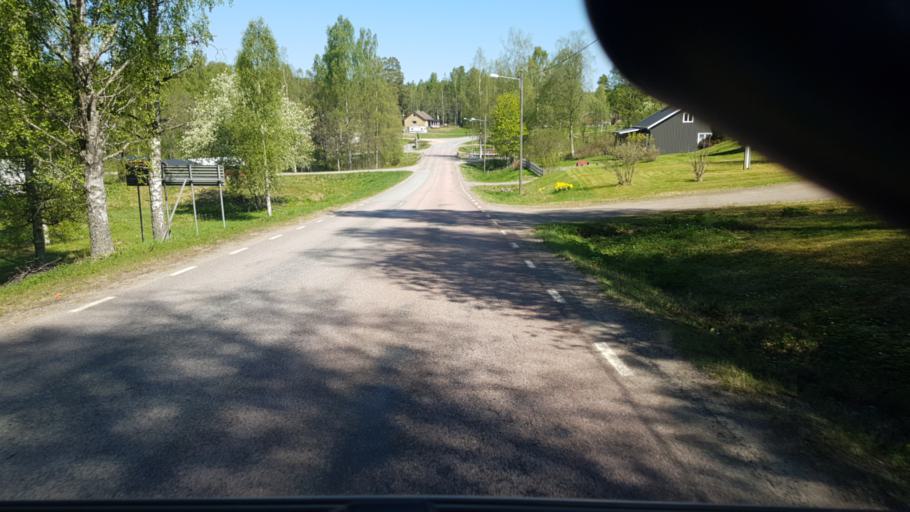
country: SE
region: Vaermland
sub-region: Arvika Kommun
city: Arvika
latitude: 59.9337
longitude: 12.6677
